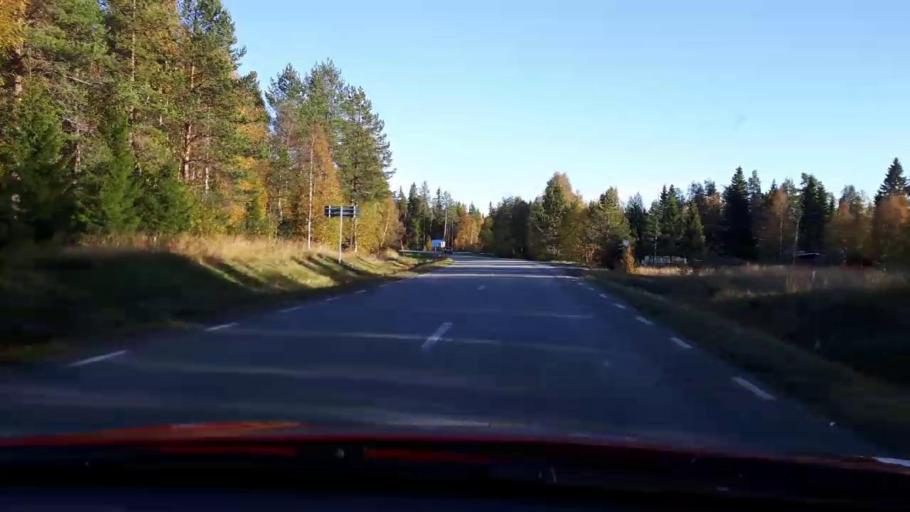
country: SE
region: Jaemtland
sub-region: OEstersunds Kommun
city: Lit
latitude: 63.7370
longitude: 14.7409
